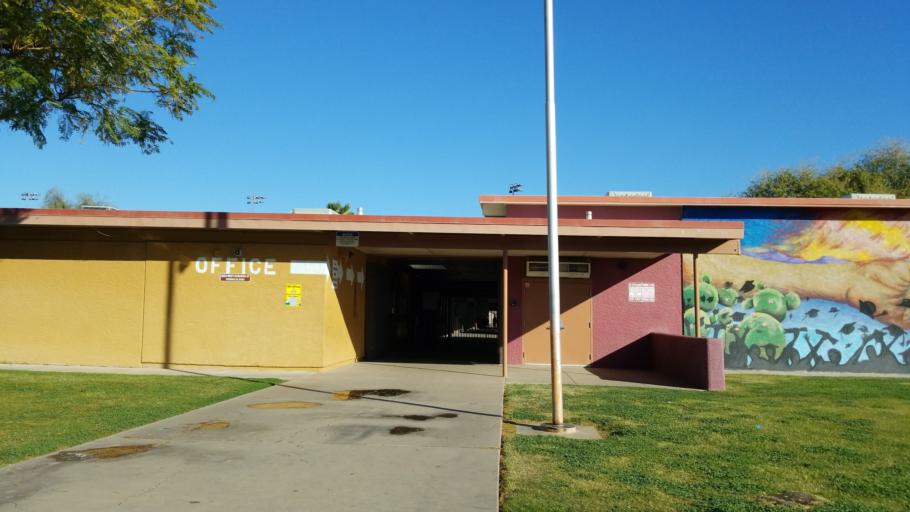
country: US
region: Arizona
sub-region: Maricopa County
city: Phoenix
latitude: 33.4297
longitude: -112.1028
